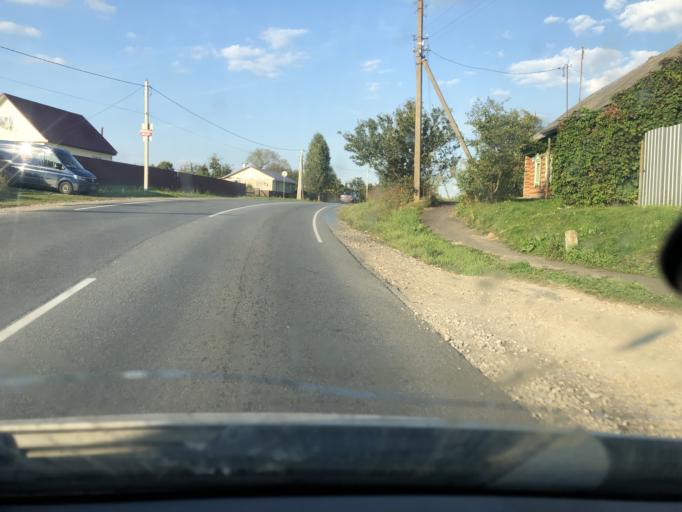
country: RU
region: Kaluga
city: Peremyshl'
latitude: 54.2293
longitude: 36.0543
